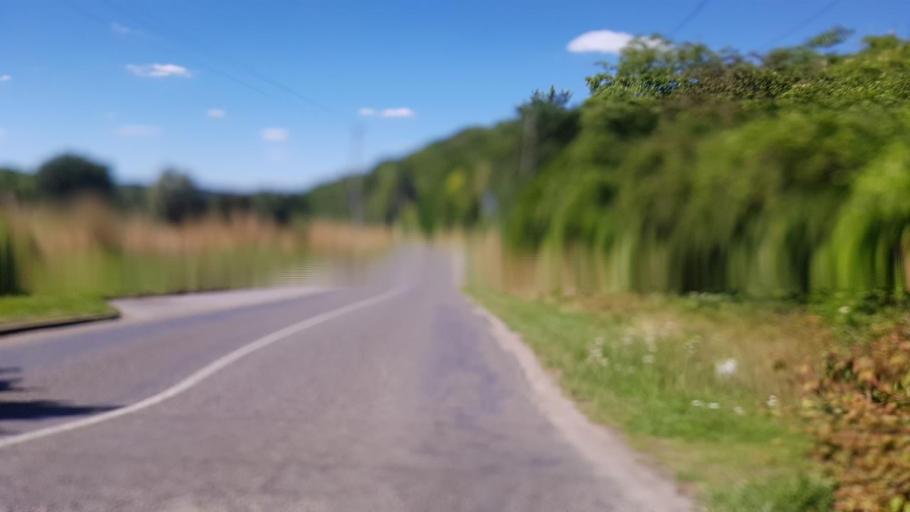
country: FR
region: Ile-de-France
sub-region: Departement de Seine-et-Marne
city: Saacy-sur-Marne
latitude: 48.9743
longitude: 3.2128
